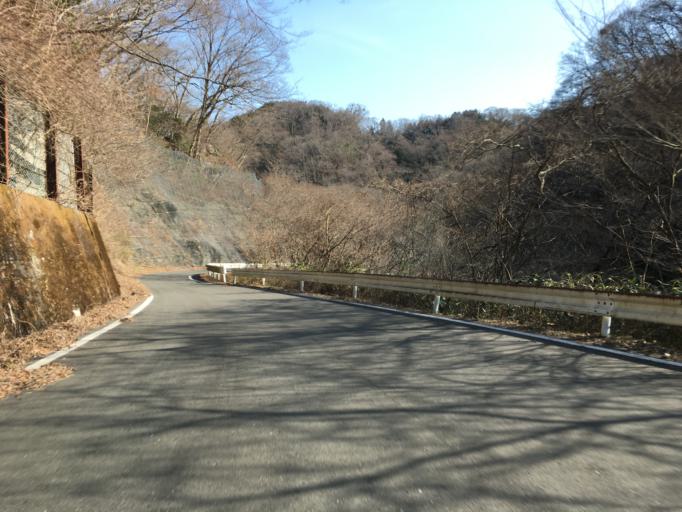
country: JP
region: Ibaraki
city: Kitaibaraki
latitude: 36.7892
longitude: 140.6564
